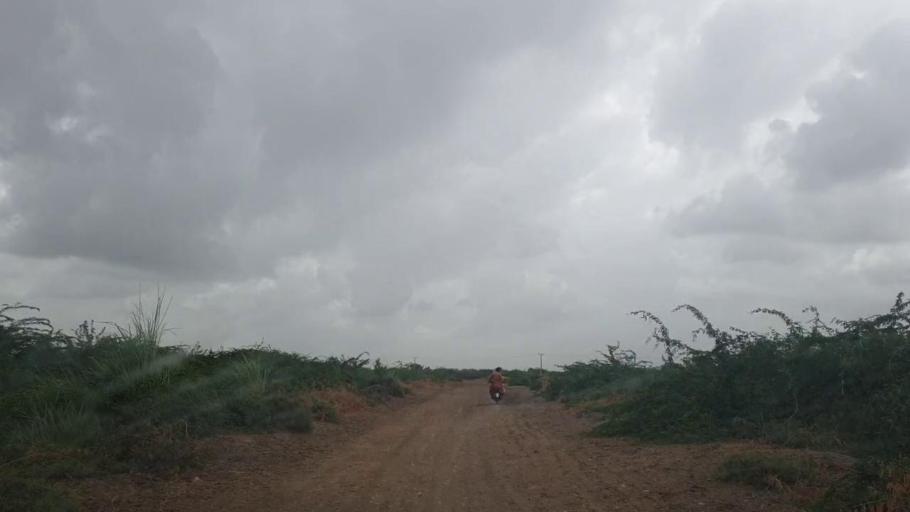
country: PK
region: Sindh
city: Naukot
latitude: 24.8554
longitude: 69.2041
